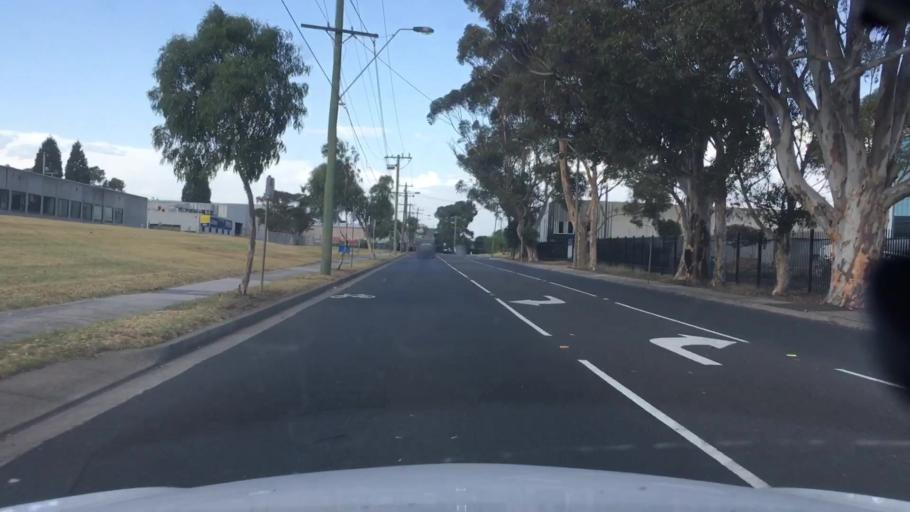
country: AU
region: Victoria
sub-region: Greater Dandenong
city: Noble Park North
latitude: -37.9523
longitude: 145.1813
